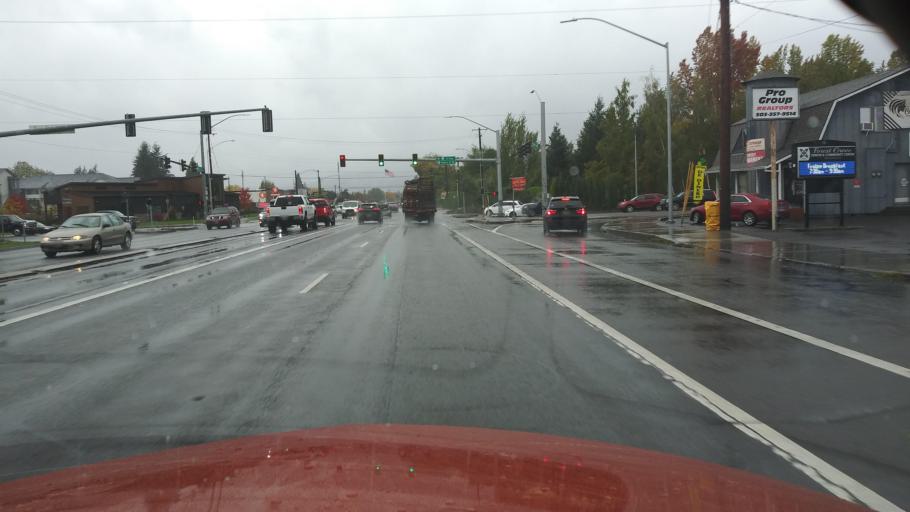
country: US
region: Oregon
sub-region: Washington County
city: Cornelius
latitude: 45.5203
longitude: -123.0833
